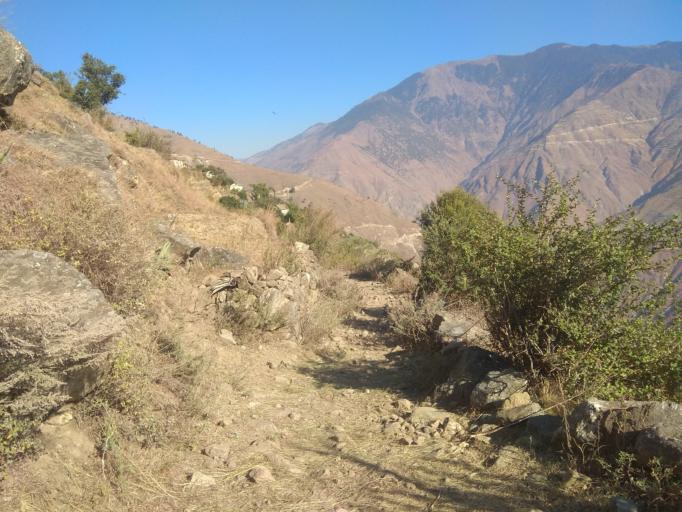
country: NP
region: Mid Western
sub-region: Karnali Zone
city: Jumla
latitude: 29.3167
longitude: 81.7413
